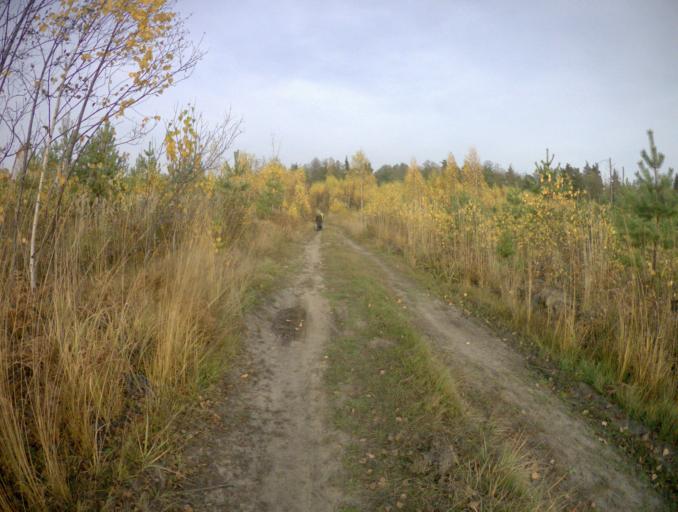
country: RU
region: Vladimir
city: Sobinka
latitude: 55.9801
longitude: 40.0691
